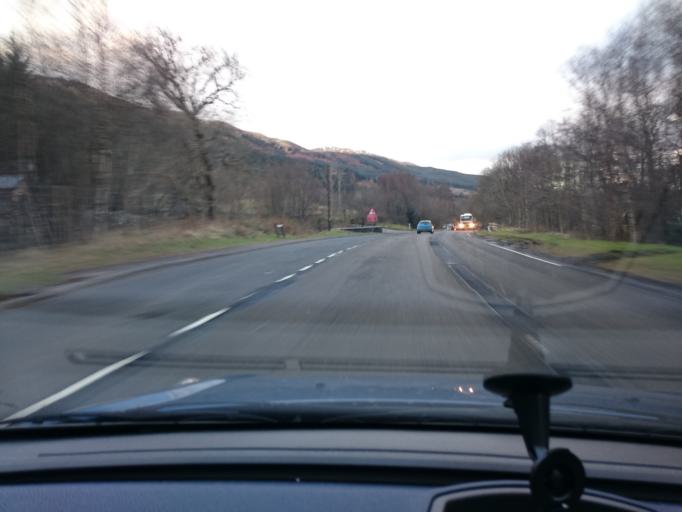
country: GB
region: Scotland
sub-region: Stirling
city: Callander
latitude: 56.2948
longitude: -4.2914
